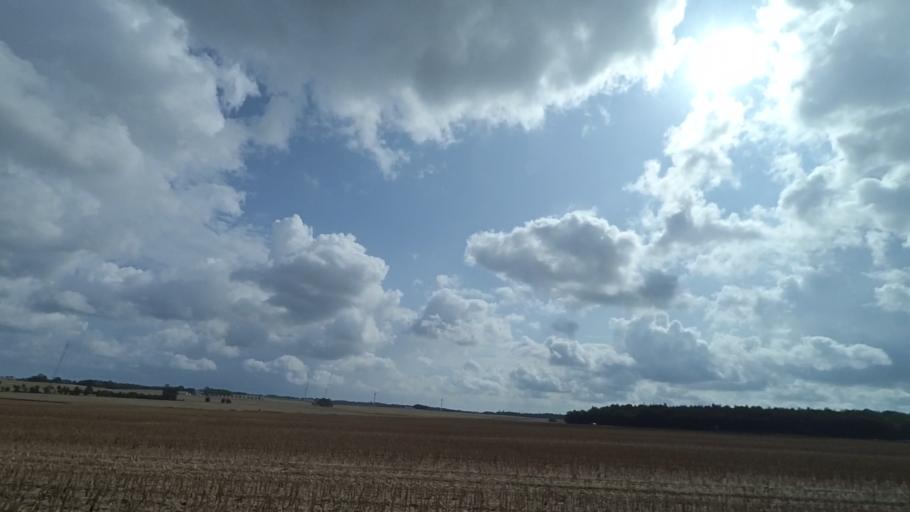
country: DK
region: Central Jutland
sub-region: Norddjurs Kommune
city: Auning
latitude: 56.4904
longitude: 10.4432
